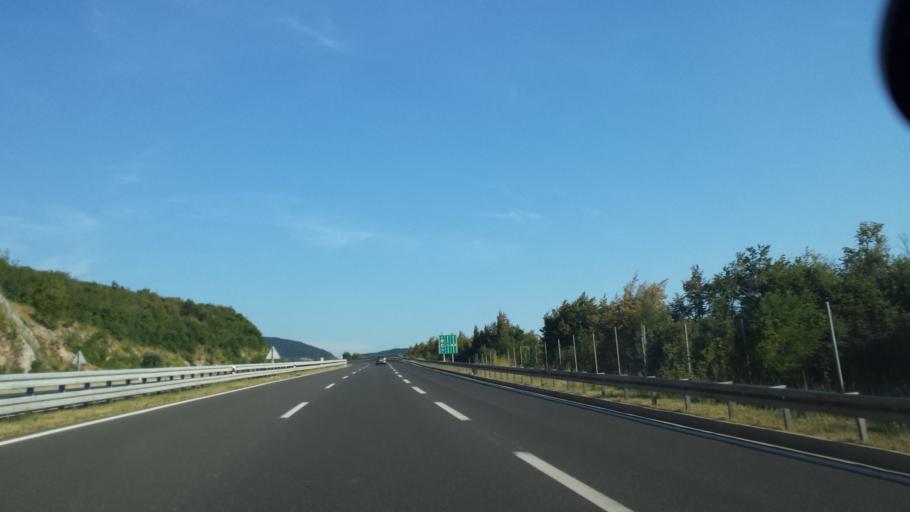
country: HR
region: Primorsko-Goranska
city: Krasica
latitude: 45.3583
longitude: 14.5769
